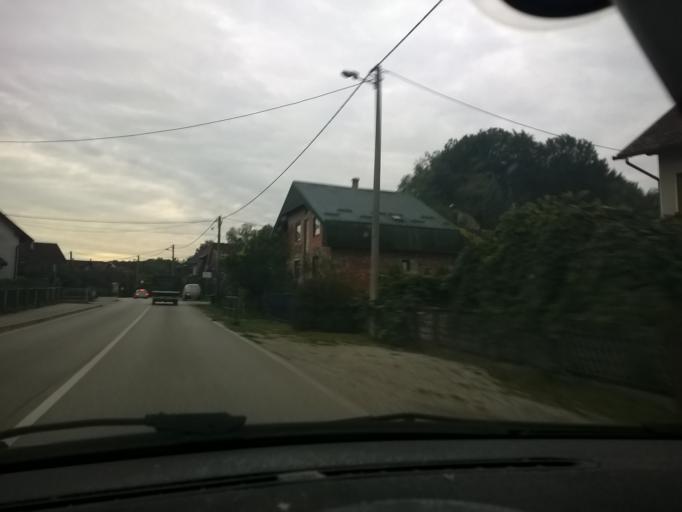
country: HR
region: Zagrebacka
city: Pojatno
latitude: 45.9051
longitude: 15.8029
